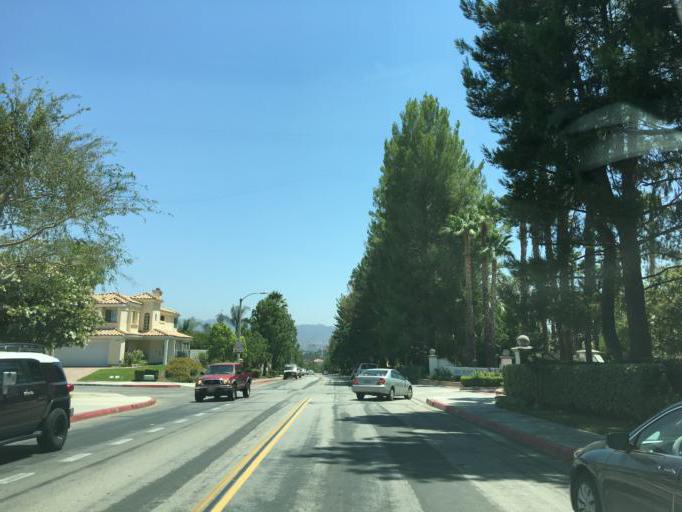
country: US
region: California
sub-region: Los Angeles County
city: Santa Clarita
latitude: 34.3900
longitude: -118.5783
